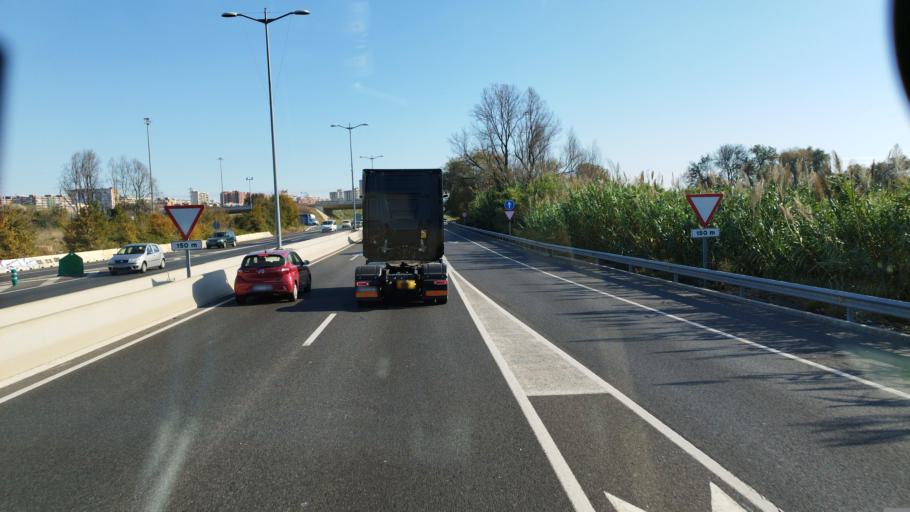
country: ES
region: Catalonia
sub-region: Provincia de Tarragona
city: Tarragona
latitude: 41.1210
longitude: 1.2255
